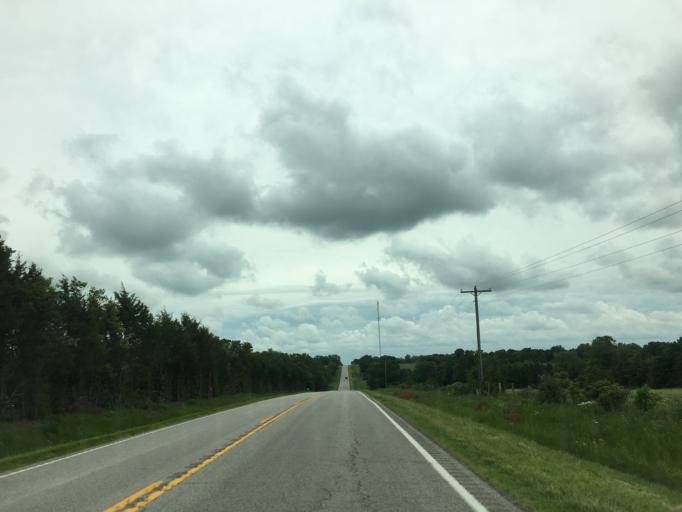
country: US
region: Missouri
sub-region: Gasconade County
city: Owensville
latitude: 38.4974
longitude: -91.4620
